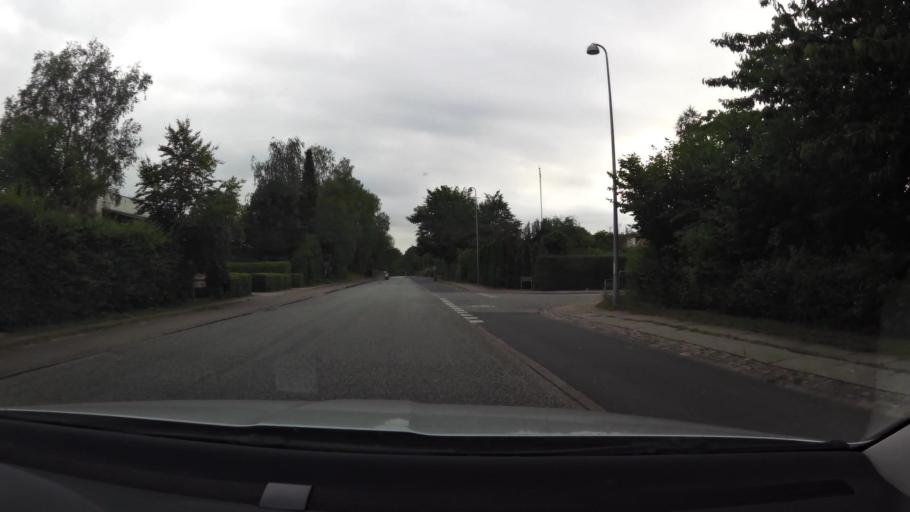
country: DK
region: Capital Region
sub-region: Lyngby-Tarbaek Kommune
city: Kongens Lyngby
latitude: 55.7986
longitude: 12.5111
